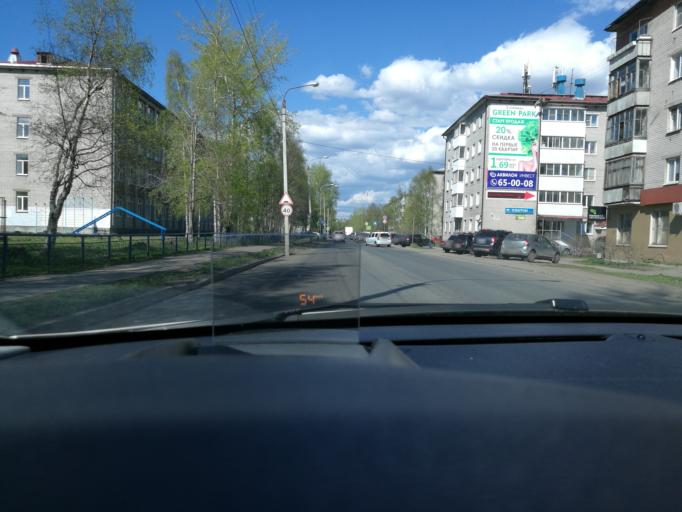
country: RU
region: Arkhangelskaya
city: Arkhangel'sk
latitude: 64.5503
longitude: 40.5359
